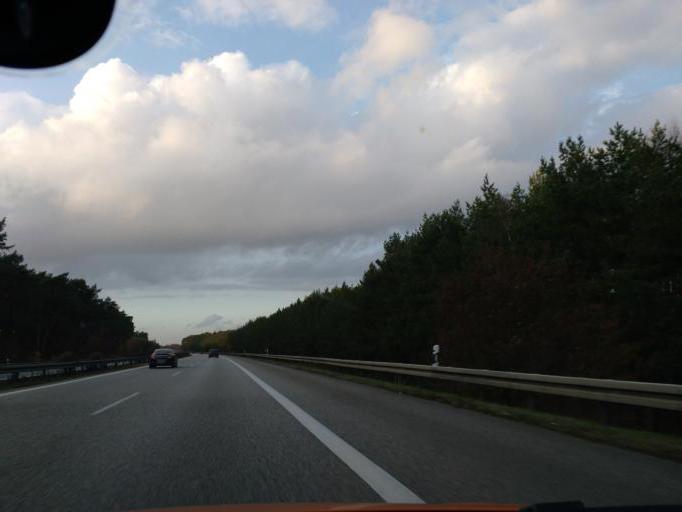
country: DE
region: Mecklenburg-Vorpommern
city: Neustadt-Glewe
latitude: 53.3867
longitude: 11.6113
